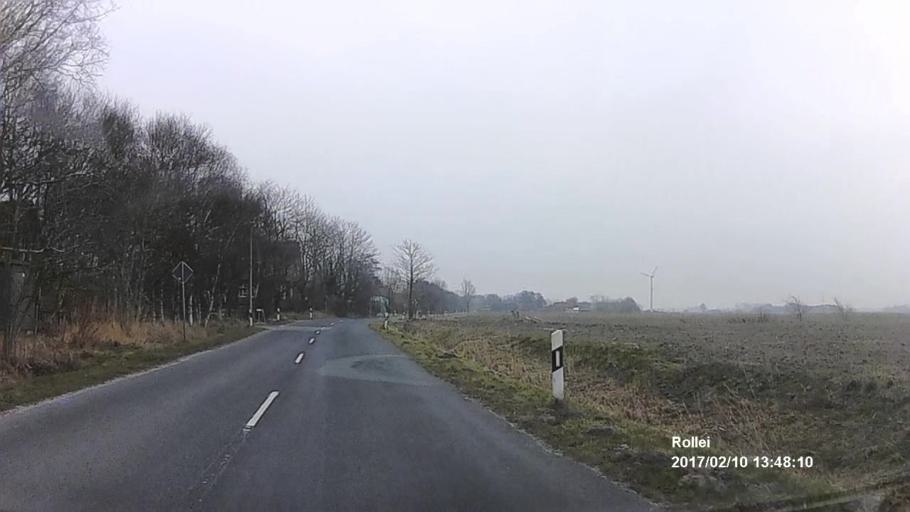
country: DE
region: Lower Saxony
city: Norddeich
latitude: 53.6017
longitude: 7.1372
